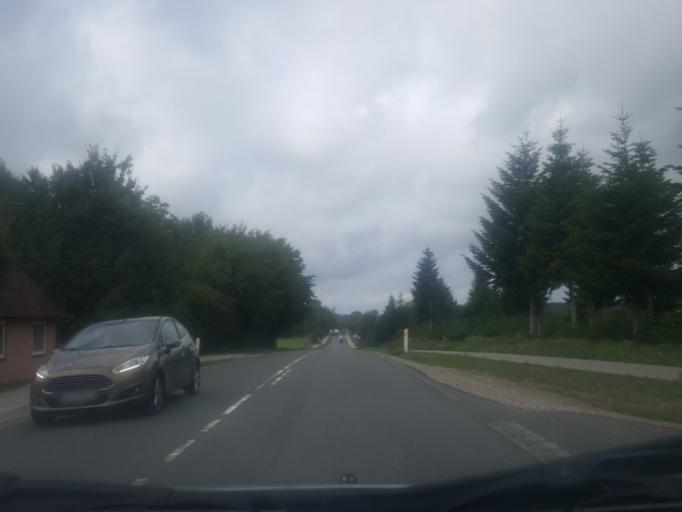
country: DK
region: Zealand
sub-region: Soro Kommune
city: Dianalund
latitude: 55.4865
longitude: 11.5198
